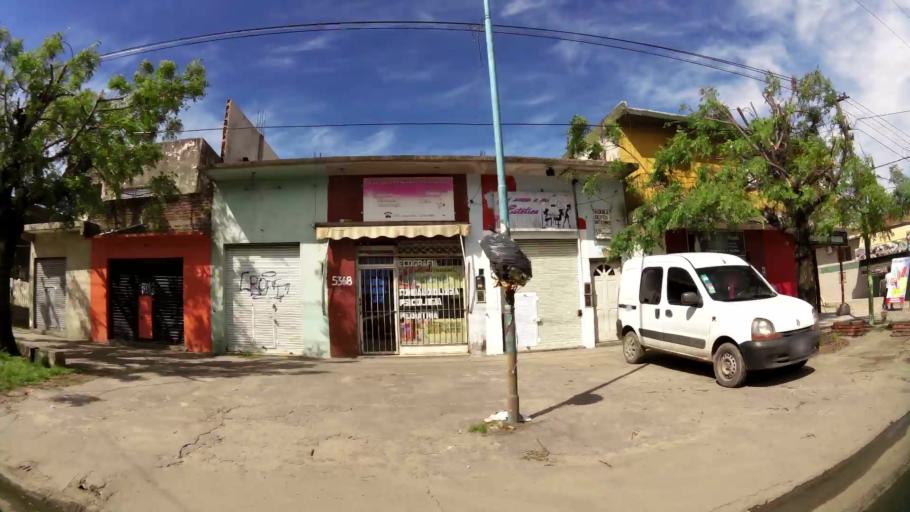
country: AR
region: Buenos Aires
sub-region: Partido de Almirante Brown
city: Adrogue
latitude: -34.7884
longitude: -58.3134
